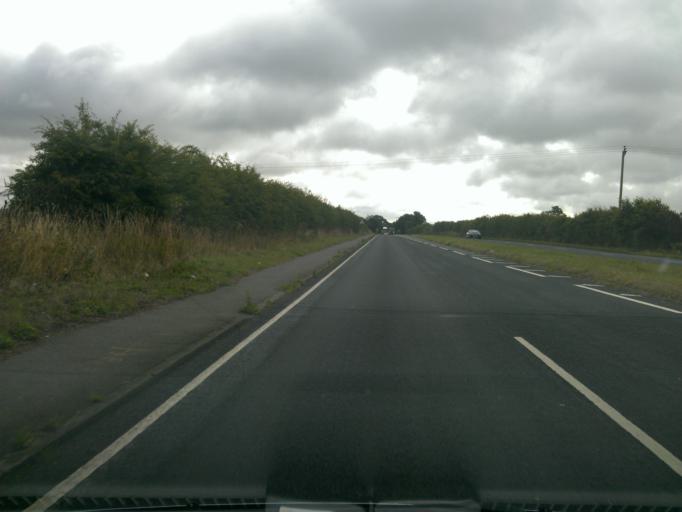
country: GB
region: England
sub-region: Essex
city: Wivenhoe
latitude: 51.8818
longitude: 0.9805
